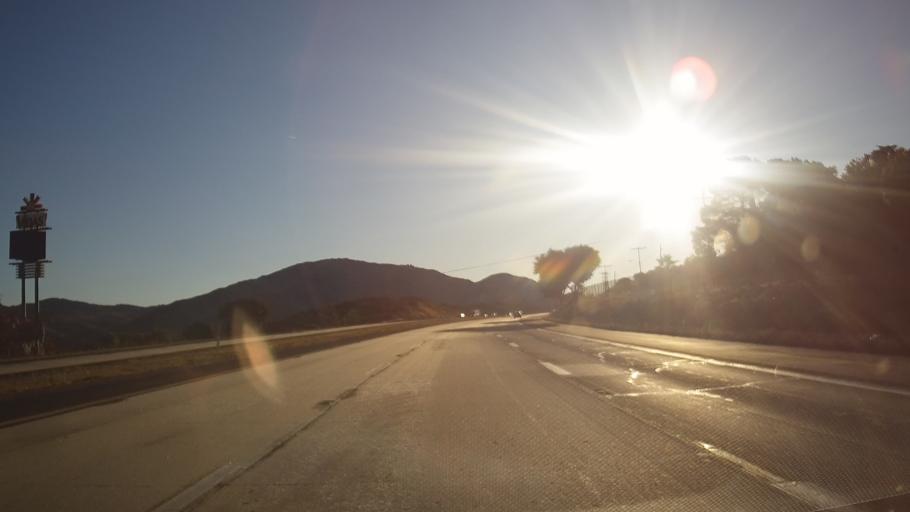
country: US
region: California
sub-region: San Diego County
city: Alpine
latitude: 32.8383
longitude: -116.7035
